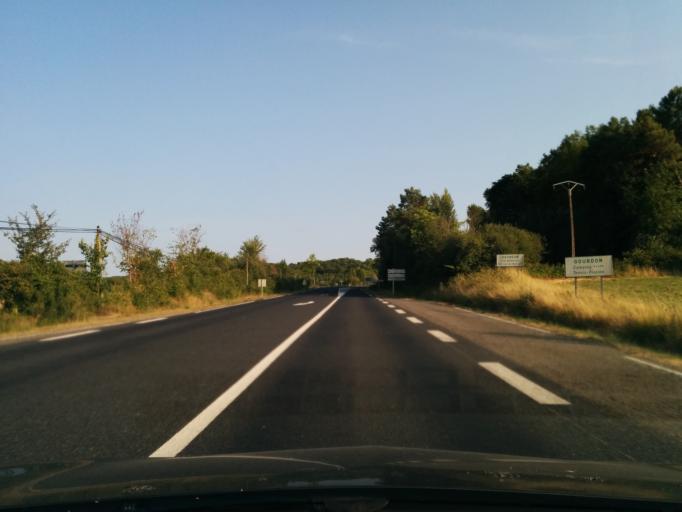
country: FR
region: Midi-Pyrenees
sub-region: Departement du Lot
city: Le Vigan
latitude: 44.7737
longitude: 1.4760
